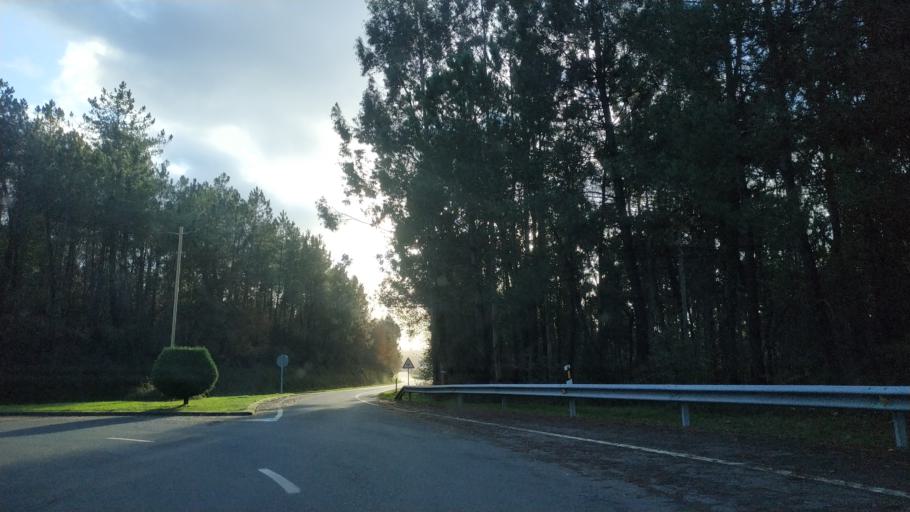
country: ES
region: Galicia
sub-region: Provincia de Pontevedra
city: Silleda
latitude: 42.7887
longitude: -8.1653
